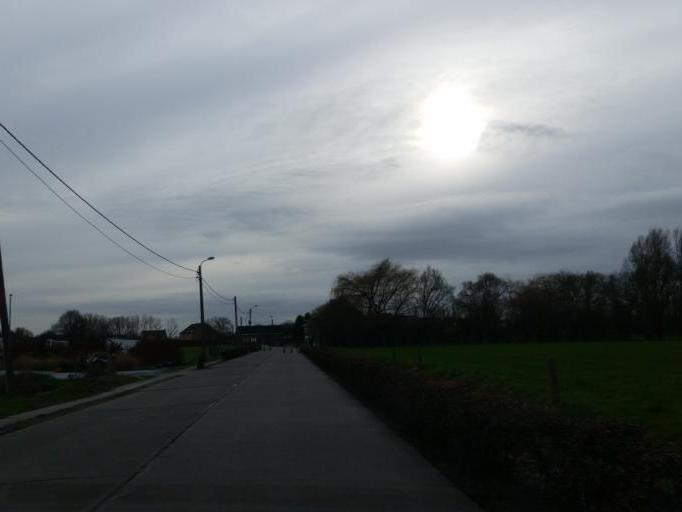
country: BE
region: Flanders
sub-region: Provincie Vlaams-Brabant
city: Zemst
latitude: 51.0017
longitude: 4.4253
